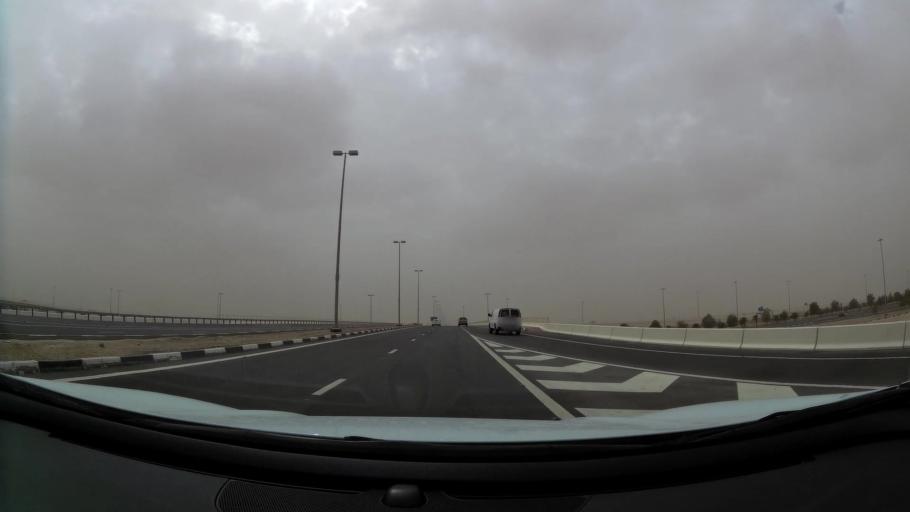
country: AE
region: Abu Dhabi
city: Abu Dhabi
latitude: 24.4158
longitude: 54.7144
